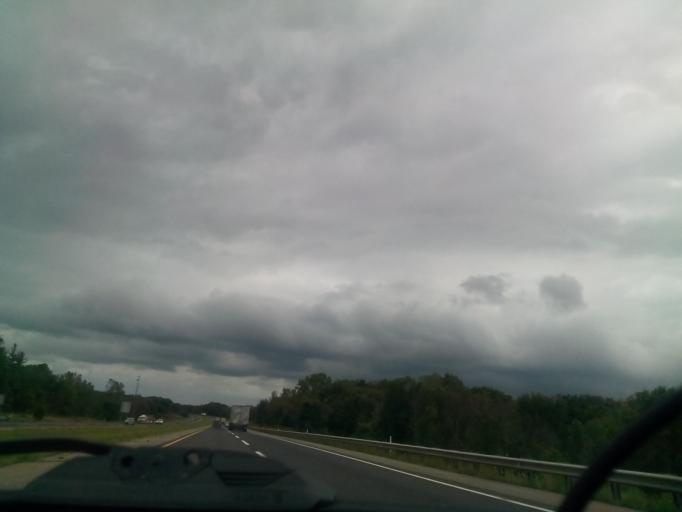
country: US
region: Indiana
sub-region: Steuben County
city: Fremont
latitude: 41.6569
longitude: -84.8444
